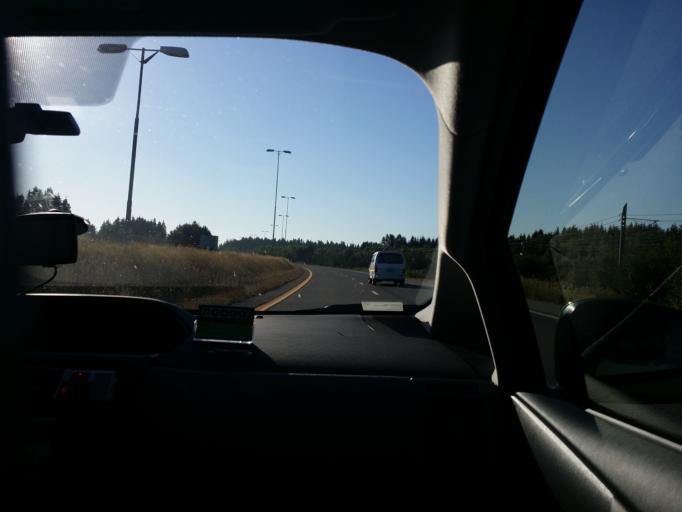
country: NO
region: Akershus
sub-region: Ullensaker
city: Jessheim
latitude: 60.1695
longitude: 11.1061
